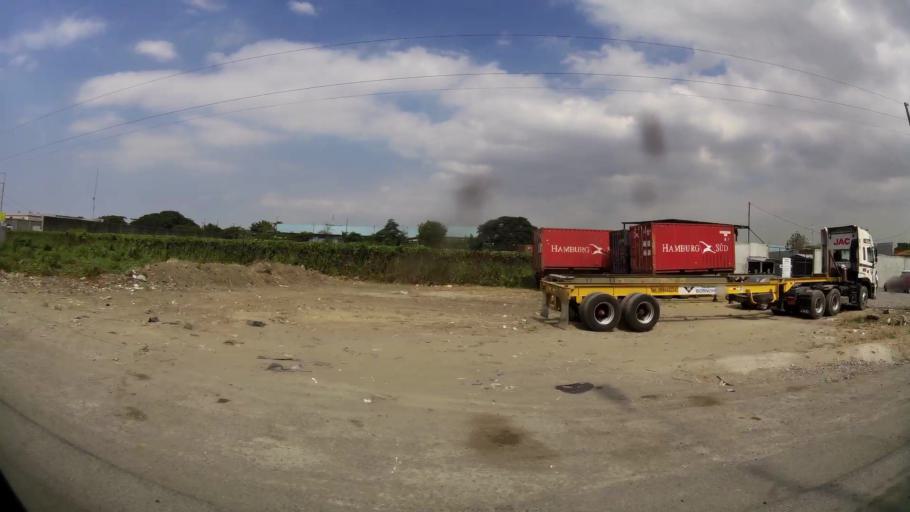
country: EC
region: Guayas
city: Santa Lucia
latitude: -2.0855
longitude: -79.9451
